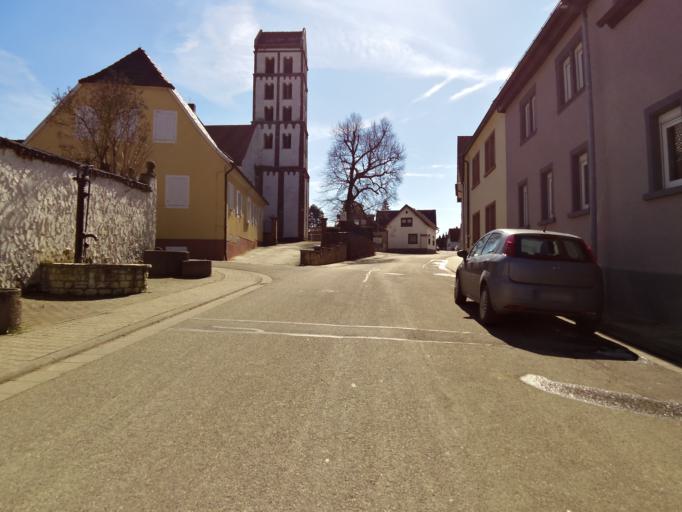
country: DE
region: Rheinland-Pfalz
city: Obrigheim
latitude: 49.5876
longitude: 8.2051
